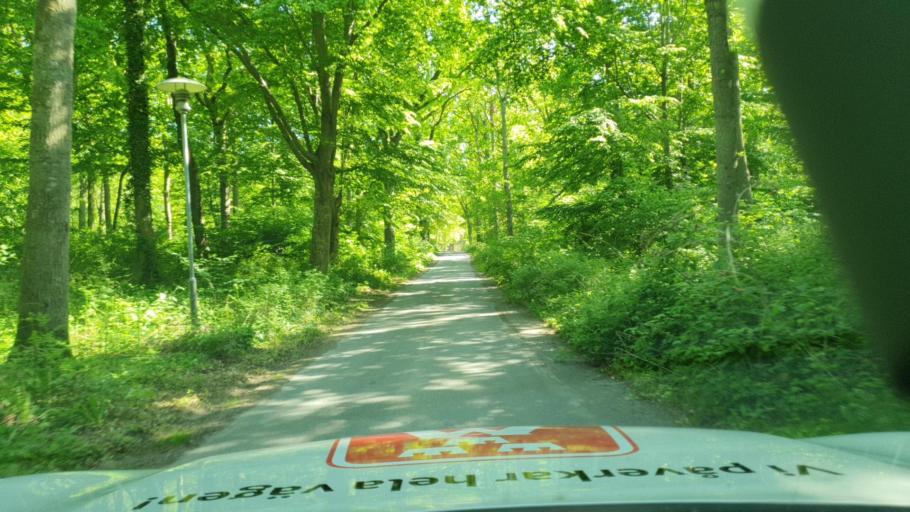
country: SE
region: Skane
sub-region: Simrishamns Kommun
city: Simrishamn
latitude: 55.4965
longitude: 14.2756
